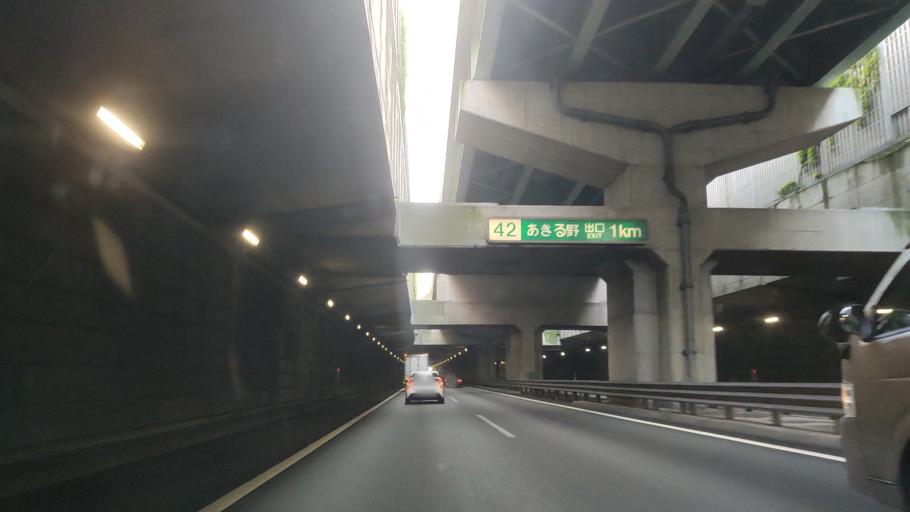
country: JP
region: Tokyo
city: Fussa
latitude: 35.7271
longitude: 139.2837
